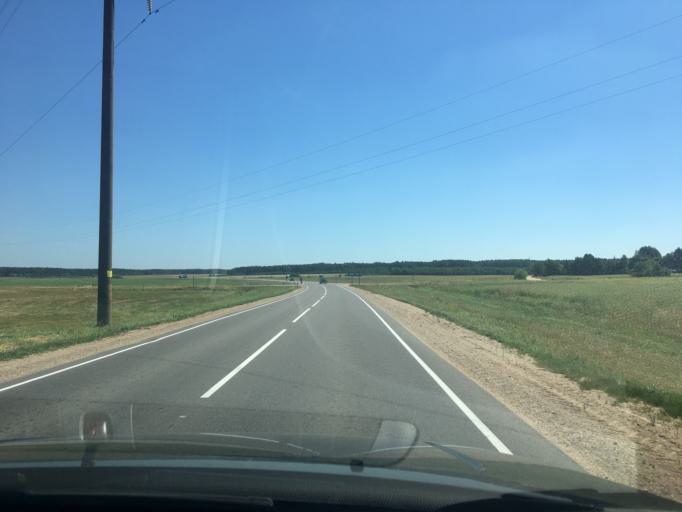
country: BY
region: Grodnenskaya
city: Iwye
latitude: 53.9134
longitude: 25.7716
